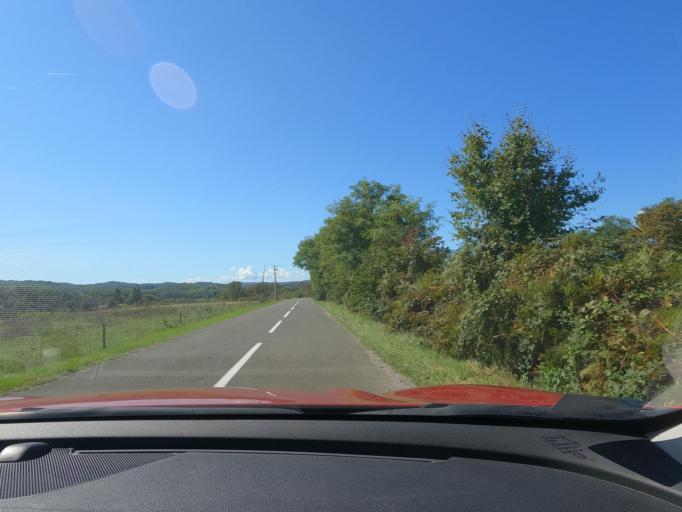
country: HR
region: Sisacko-Moslavacka
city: Petrinja
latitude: 45.3278
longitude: 16.2352
